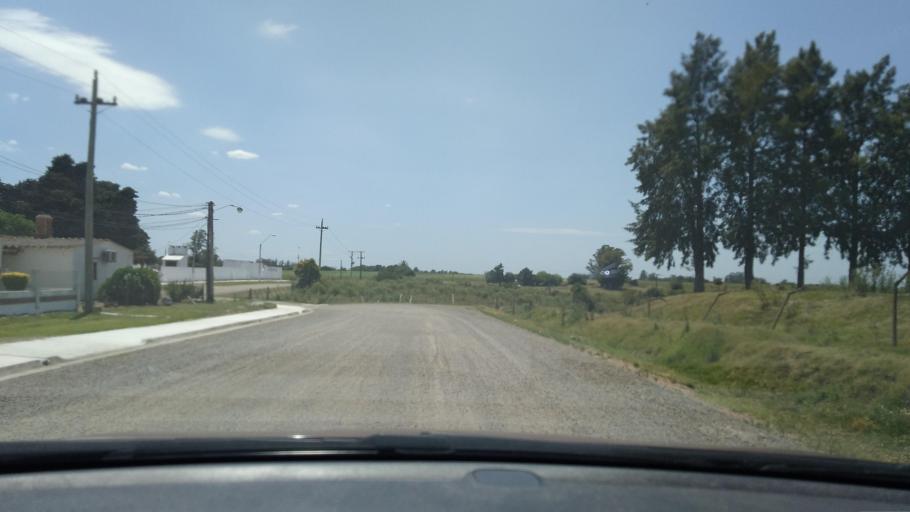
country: UY
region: Canelones
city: Tala
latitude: -34.2054
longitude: -55.7417
